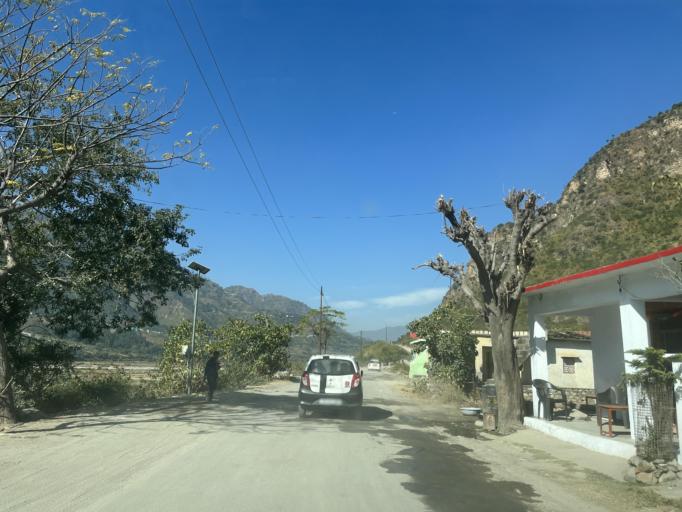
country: IN
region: Uttarakhand
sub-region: Naini Tal
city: Naini Tal
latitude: 29.5082
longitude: 79.4447
